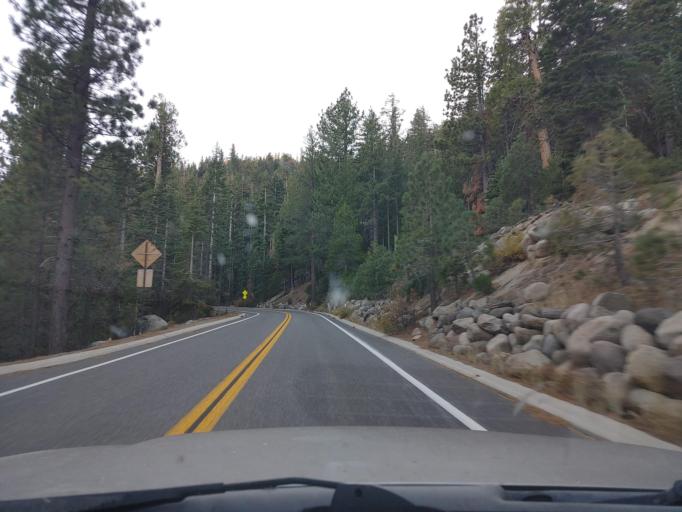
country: US
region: California
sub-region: Placer County
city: Tahoma
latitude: 38.9854
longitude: -120.1082
